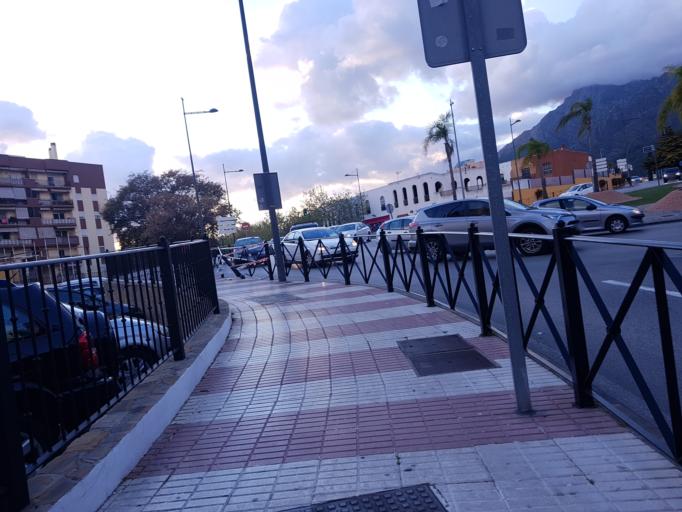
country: ES
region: Andalusia
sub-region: Provincia de Malaga
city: Marbella
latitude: 36.5176
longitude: -4.8895
